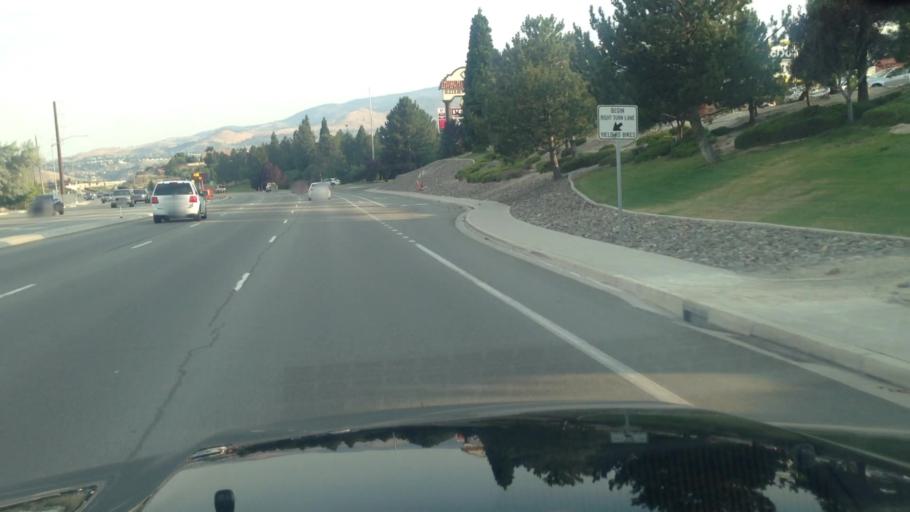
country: US
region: Nevada
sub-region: Washoe County
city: Reno
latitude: 39.5325
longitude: -119.8648
